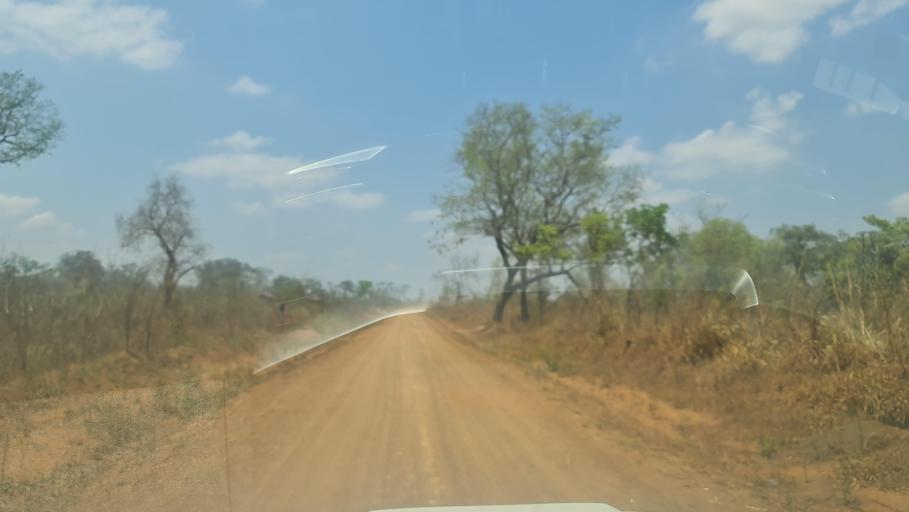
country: MW
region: Southern Region
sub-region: Nsanje District
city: Nsanje
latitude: -17.4113
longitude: 35.8147
